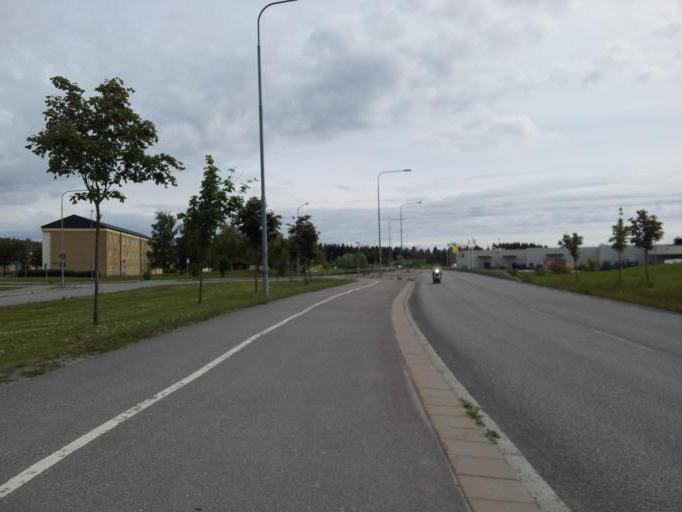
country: SE
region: Uppsala
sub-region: Uppsala Kommun
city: Gamla Uppsala
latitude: 59.8851
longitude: 17.6562
